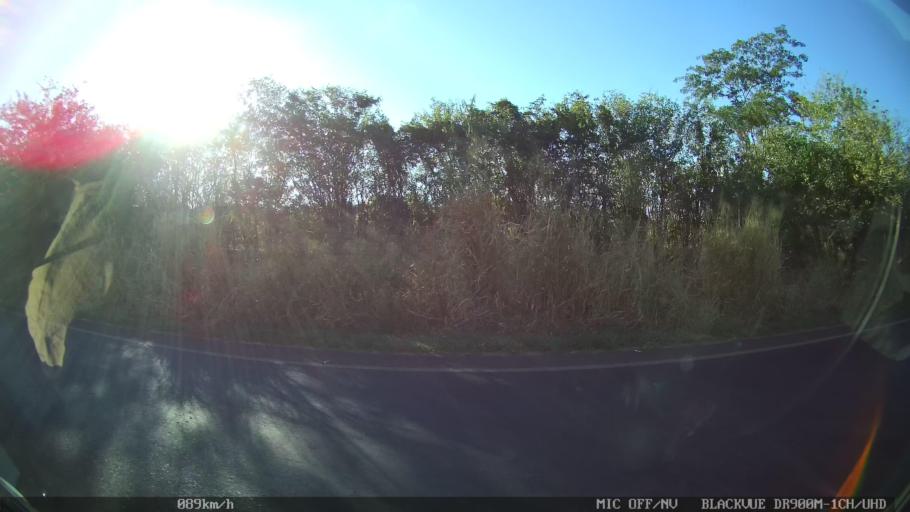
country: BR
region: Sao Paulo
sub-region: Guapiacu
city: Guapiacu
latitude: -20.7477
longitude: -49.1242
